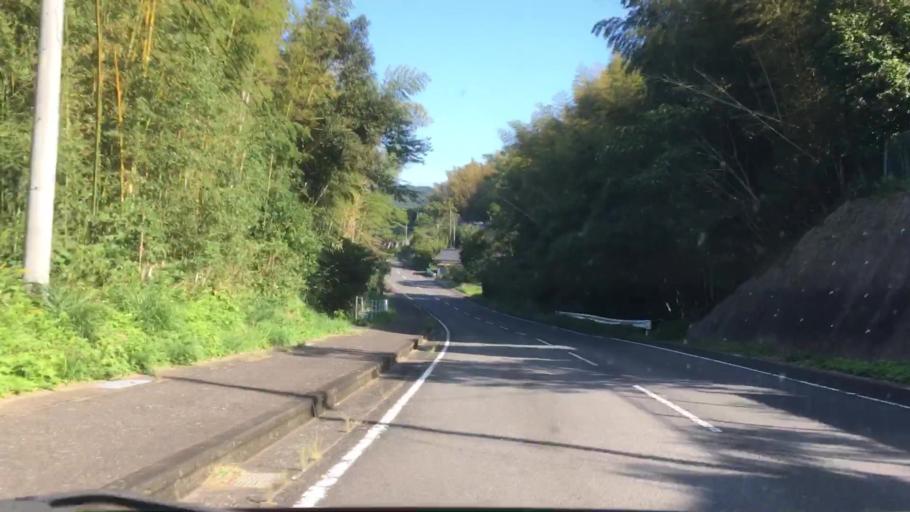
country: JP
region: Nagasaki
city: Sasebo
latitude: 33.0178
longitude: 129.6542
